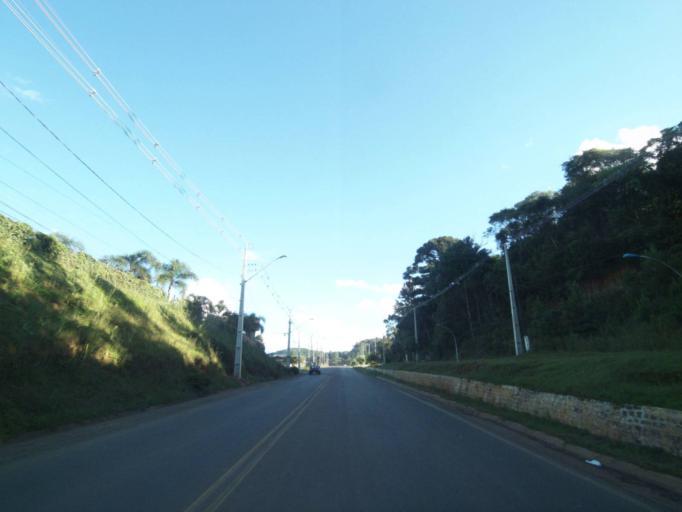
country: BR
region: Parana
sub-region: Uniao Da Vitoria
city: Uniao da Vitoria
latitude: -26.1544
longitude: -51.5428
